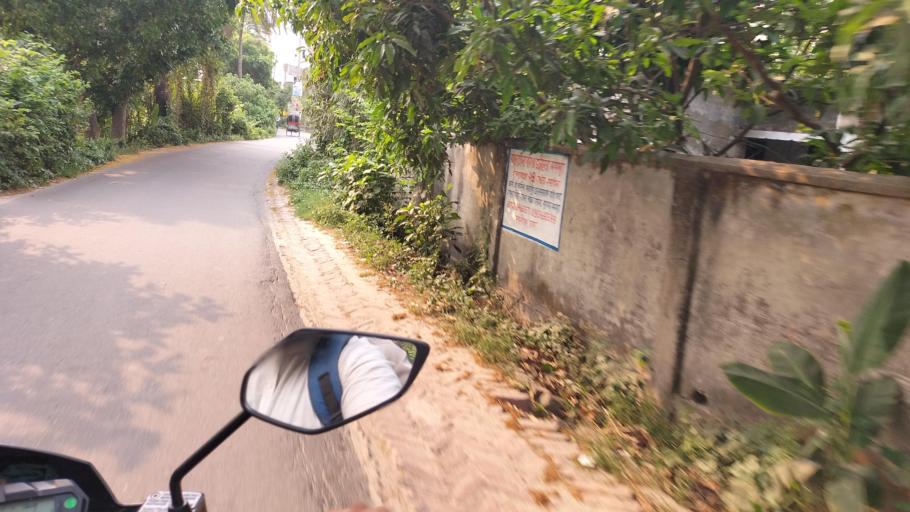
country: BD
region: Dhaka
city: Azimpur
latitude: 23.6695
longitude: 90.3460
